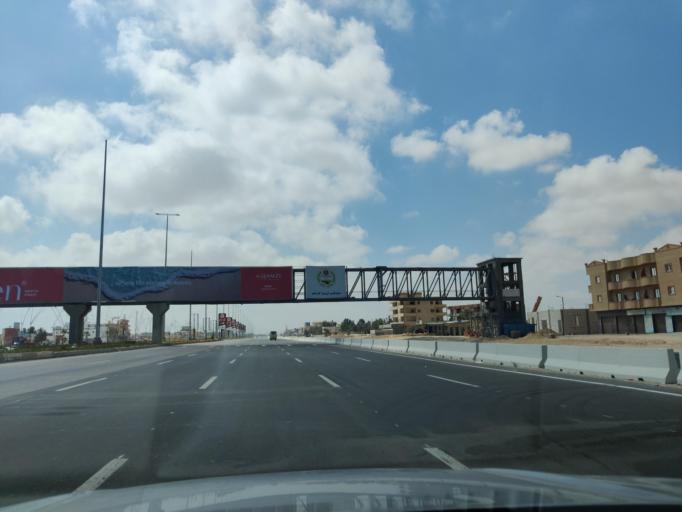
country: EG
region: Muhafazat Matruh
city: Al `Alamayn
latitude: 30.9479
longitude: 28.7750
